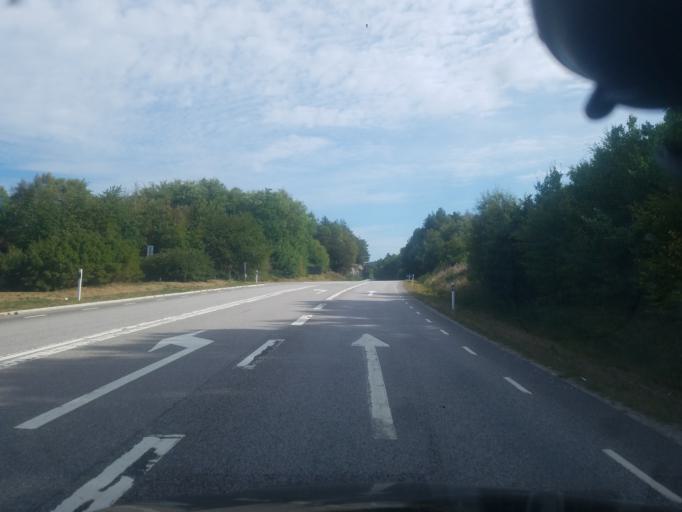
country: SE
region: Vaestra Goetaland
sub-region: Orust
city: Henan
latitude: 58.2624
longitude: 11.6805
